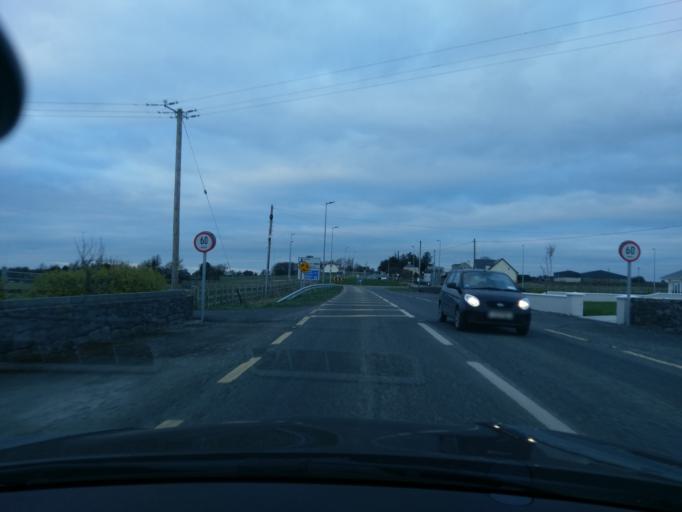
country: IE
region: Connaught
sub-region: County Galway
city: Tuam
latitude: 53.4016
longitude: -8.8297
